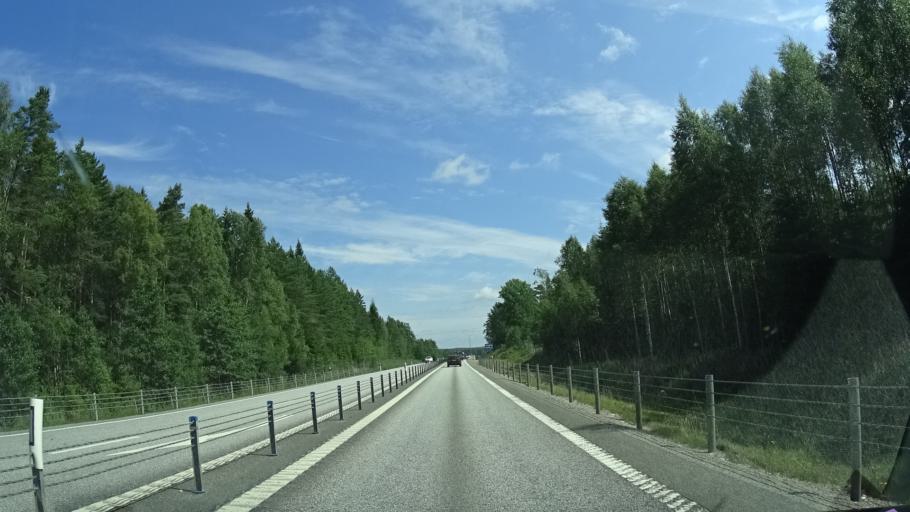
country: SE
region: OErebro
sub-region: Degerfors Kommun
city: Degerfors
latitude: 59.3202
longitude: 14.3473
